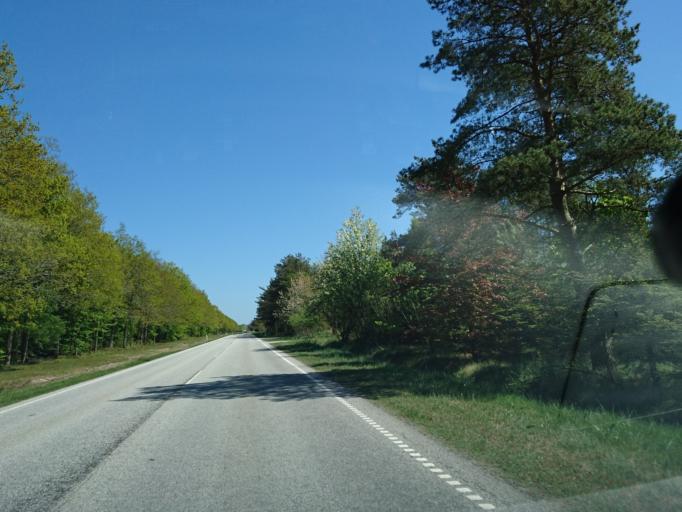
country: DK
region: North Denmark
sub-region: Hjorring Kommune
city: Sindal
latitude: 57.5878
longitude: 10.2615
